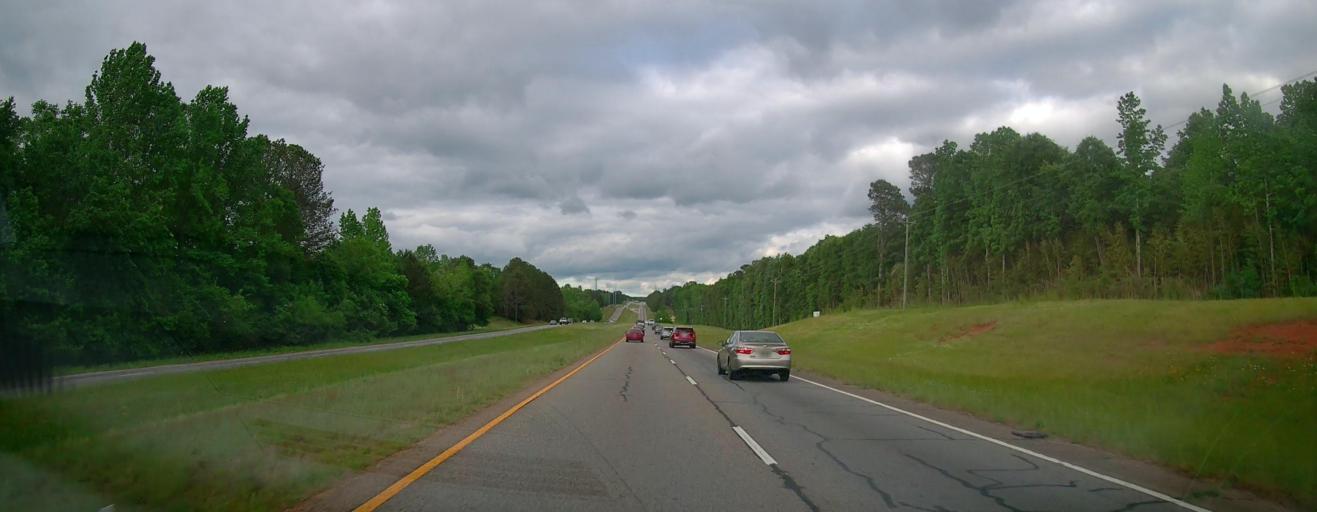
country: US
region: Georgia
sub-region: Oconee County
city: Bogart
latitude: 33.9040
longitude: -83.5687
